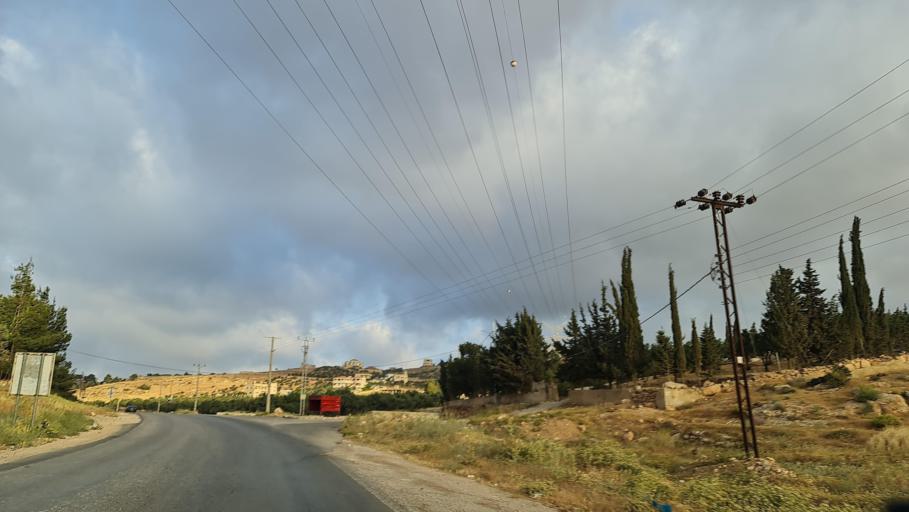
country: JO
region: Amman
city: Al Jubayhah
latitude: 32.0927
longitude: 35.9189
